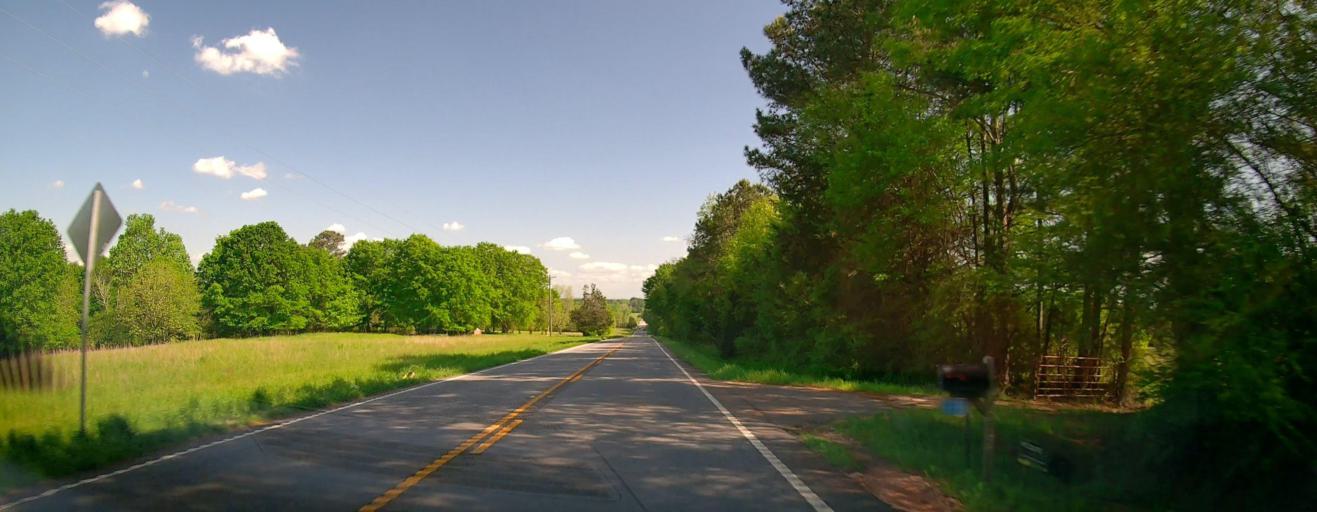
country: US
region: Georgia
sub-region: Morgan County
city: Madison
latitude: 33.6460
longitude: -83.4960
